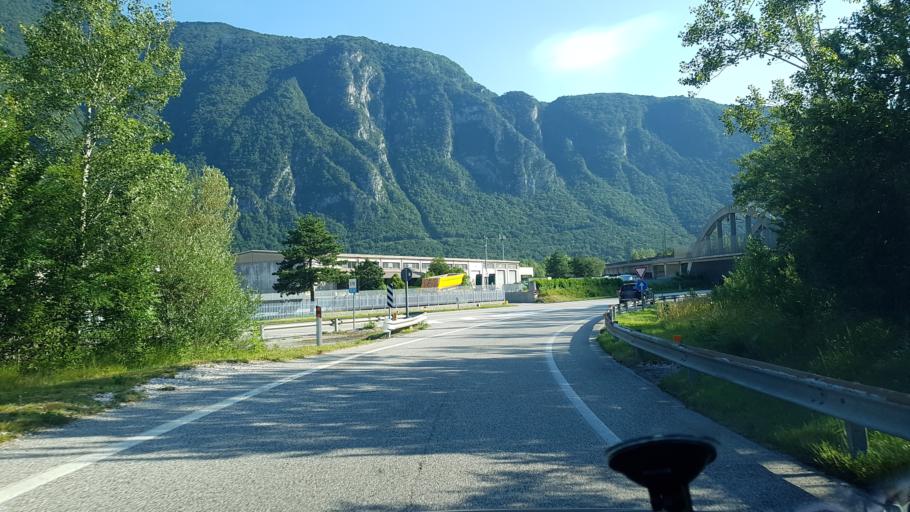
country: IT
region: Friuli Venezia Giulia
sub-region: Provincia di Udine
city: Amaro
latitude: 46.3816
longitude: 13.1343
